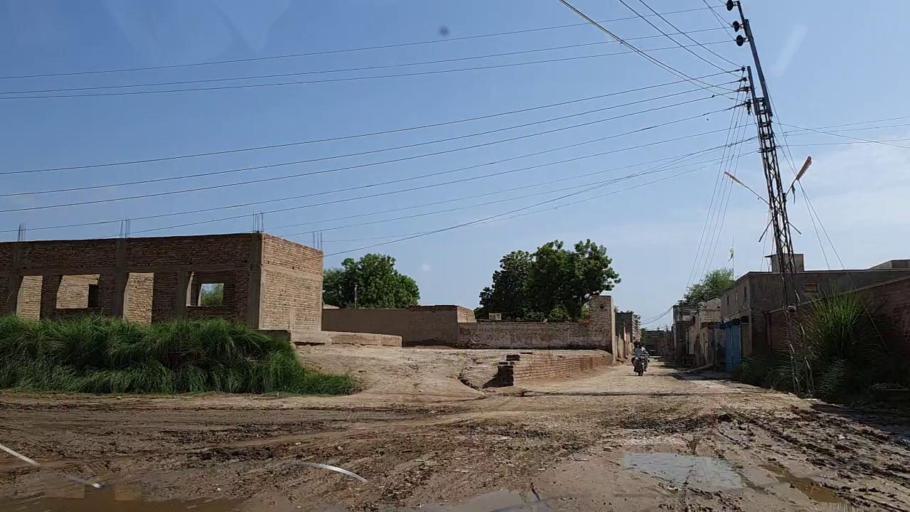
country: PK
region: Sindh
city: Pad Idan
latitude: 26.7717
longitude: 68.3017
